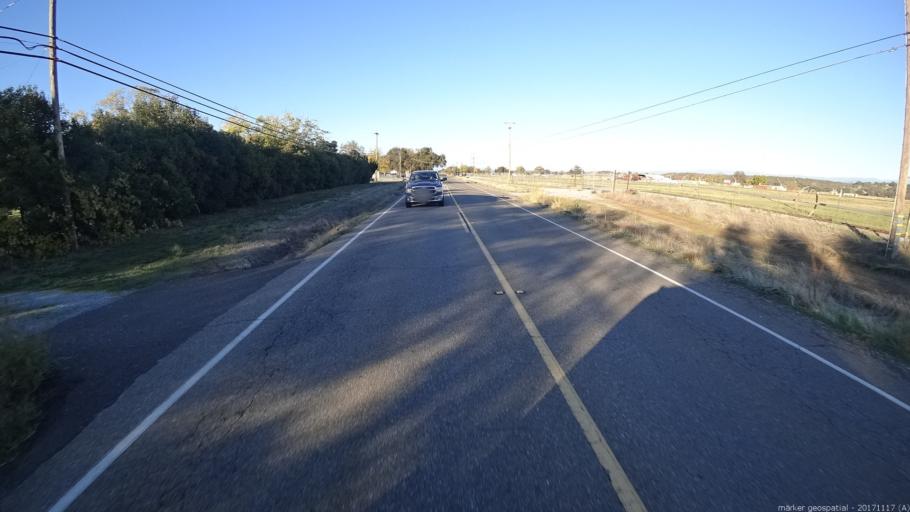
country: US
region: California
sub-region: Shasta County
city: Anderson
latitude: 40.4717
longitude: -122.2423
